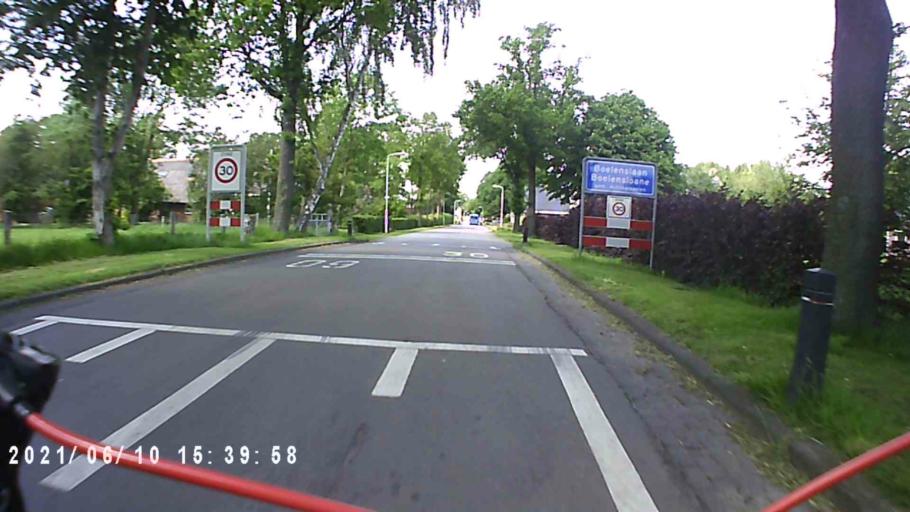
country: NL
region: Friesland
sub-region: Gemeente Achtkarspelen
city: Boelenslaan
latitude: 53.1590
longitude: 6.1476
